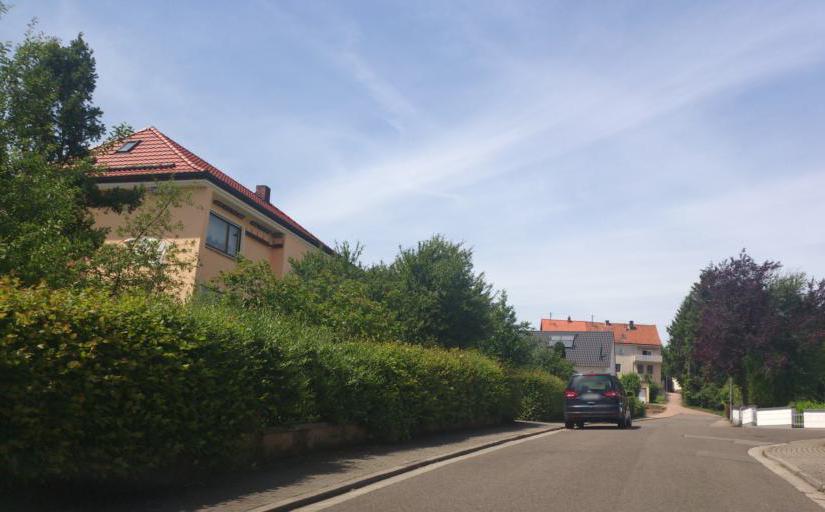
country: DE
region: Saarland
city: Bexbach
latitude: 49.3811
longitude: 7.2584
